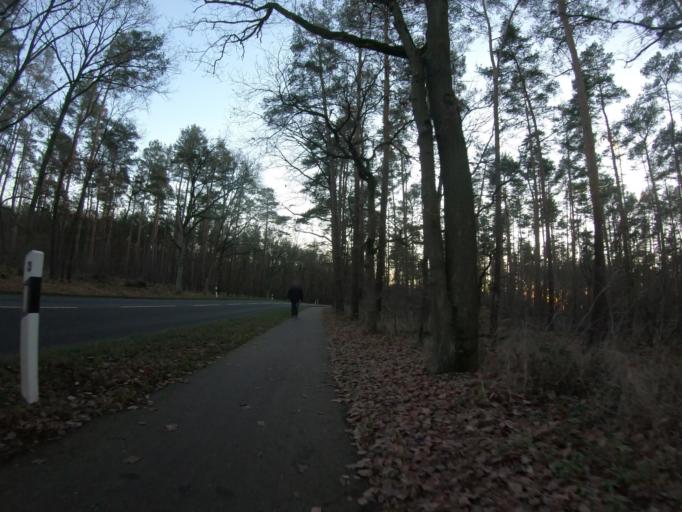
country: DE
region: Lower Saxony
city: Wagenhoff
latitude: 52.5028
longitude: 10.4809
